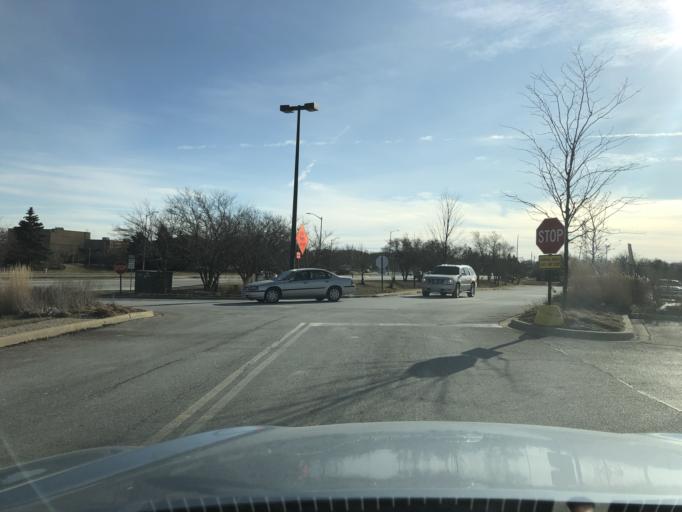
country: US
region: Illinois
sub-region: Lake County
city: Grandwood Park
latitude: 42.3811
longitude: -87.9640
